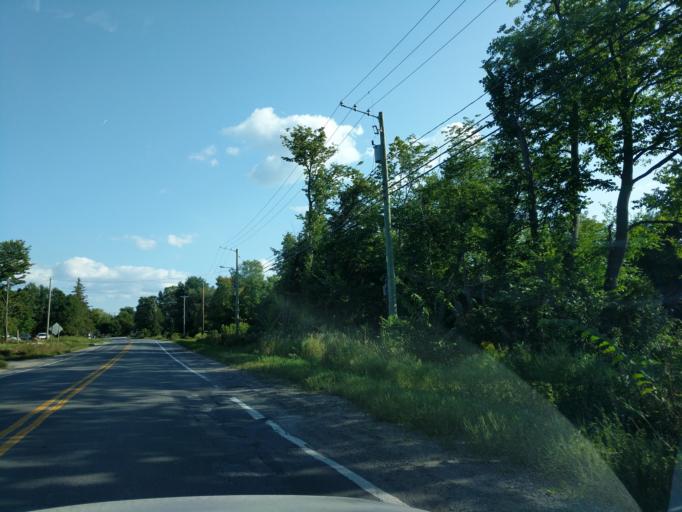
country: CA
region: Ontario
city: Bells Corners
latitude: 45.4448
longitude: -75.9199
